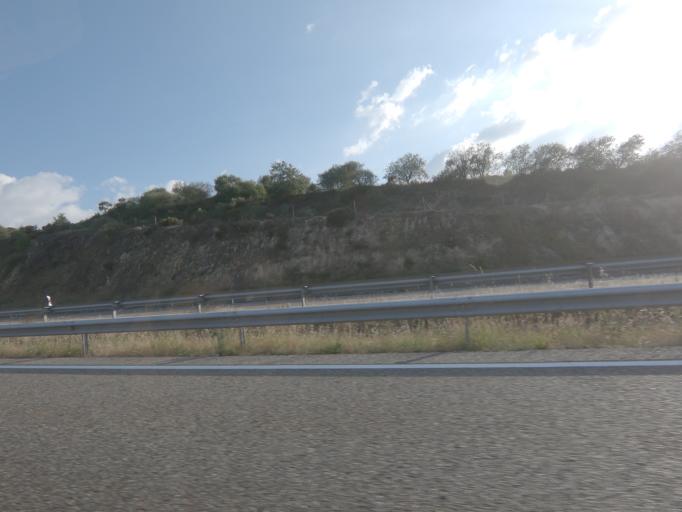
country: ES
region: Galicia
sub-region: Provincia de Ourense
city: Cualedro
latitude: 42.0011
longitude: -7.5613
